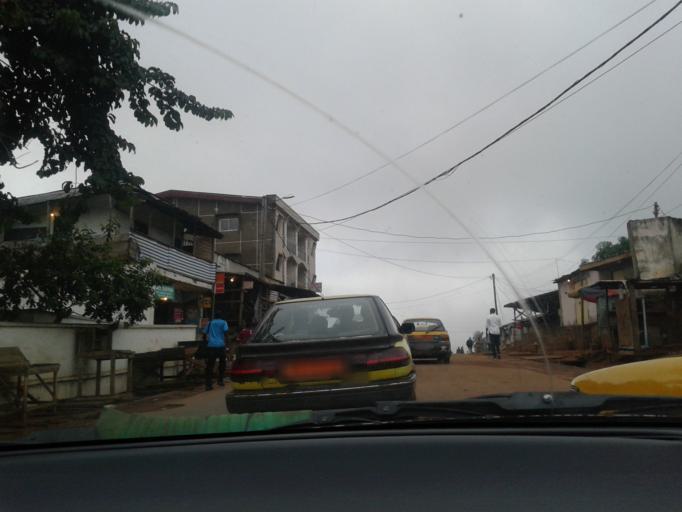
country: CM
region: Centre
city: Yaounde
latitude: 3.8866
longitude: 11.5304
